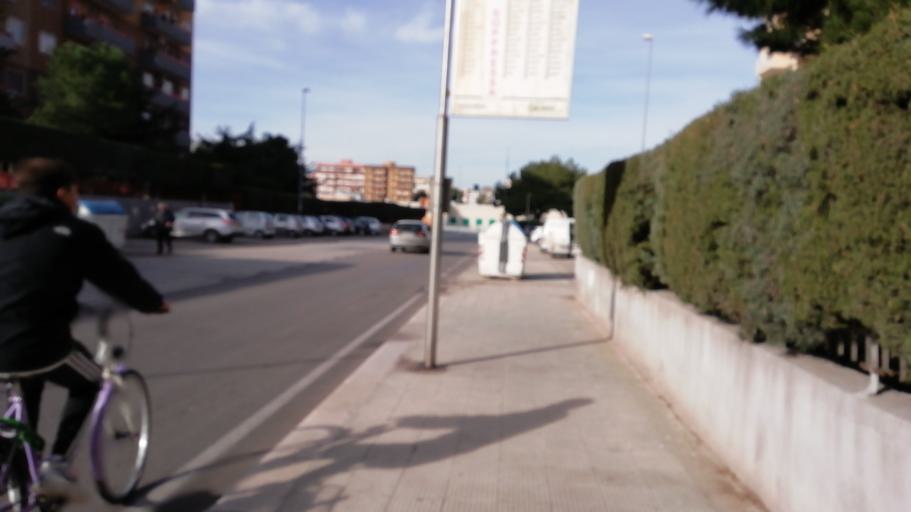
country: IT
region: Apulia
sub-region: Provincia di Bari
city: Triggiano
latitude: 41.1035
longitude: 16.9134
